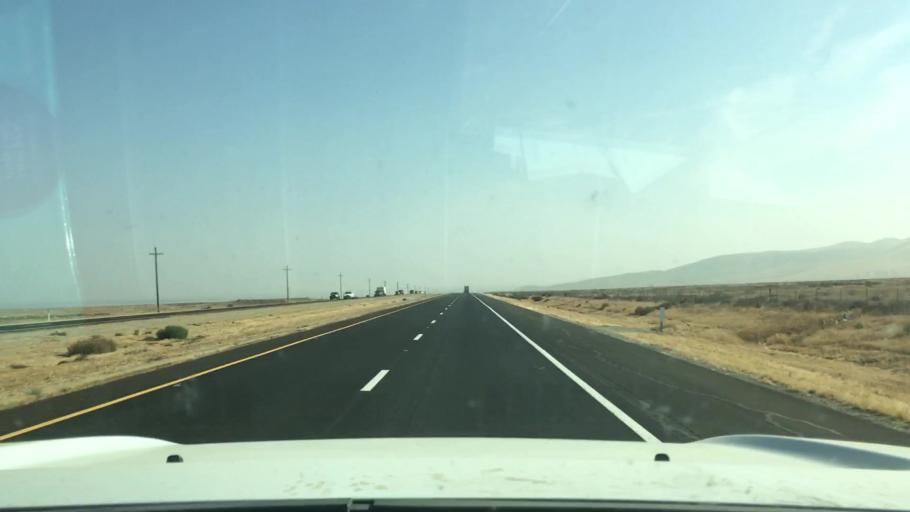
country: US
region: California
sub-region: San Luis Obispo County
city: Shandon
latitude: 35.6689
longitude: -120.0780
